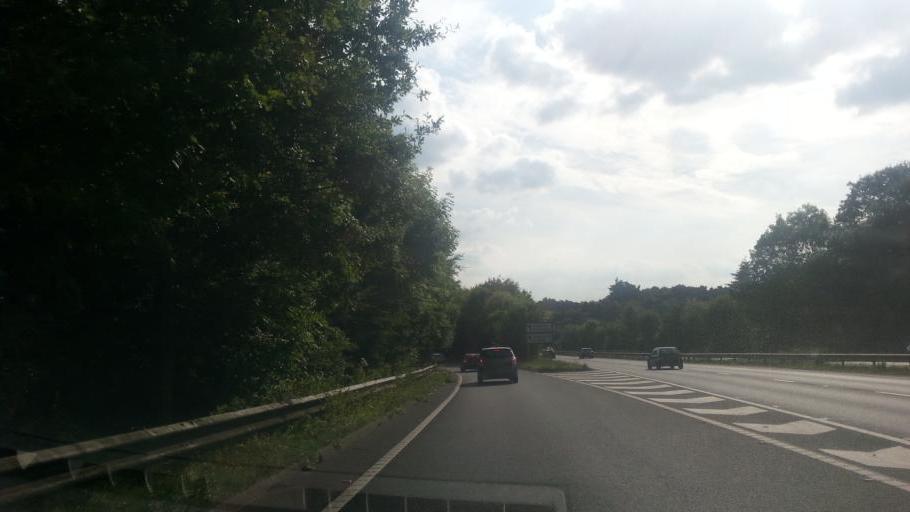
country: GB
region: England
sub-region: Surrey
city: Godalming
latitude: 51.2230
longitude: -0.6322
